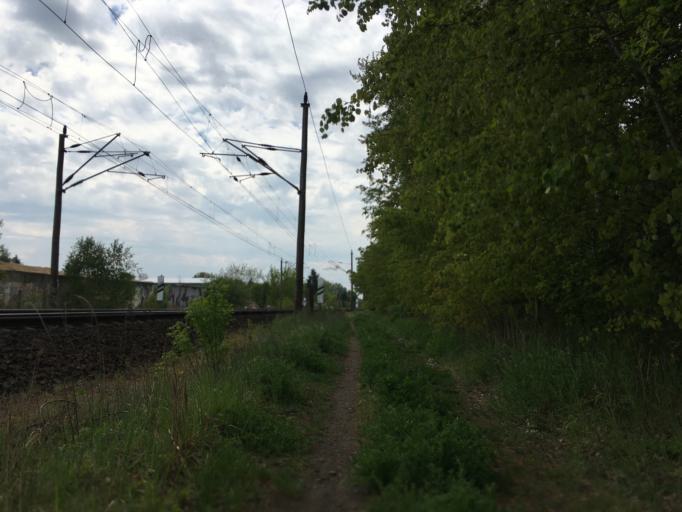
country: DE
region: Brandenburg
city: Bernau bei Berlin
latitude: 52.6888
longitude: 13.6069
